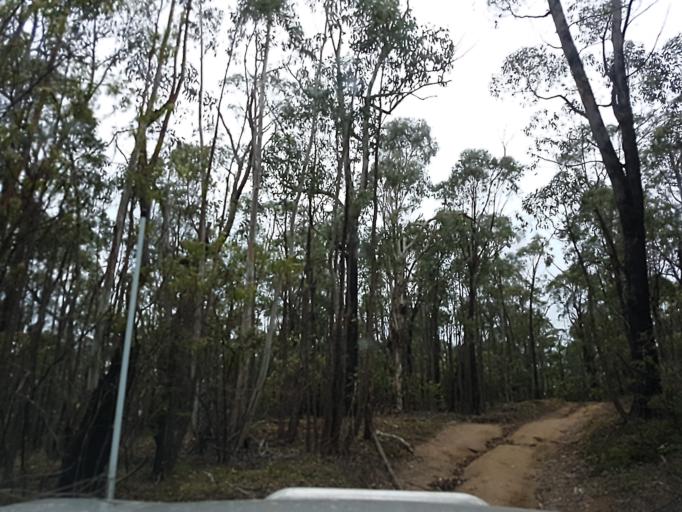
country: AU
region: New South Wales
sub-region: Snowy River
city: Jindabyne
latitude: -36.8599
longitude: 148.3300
